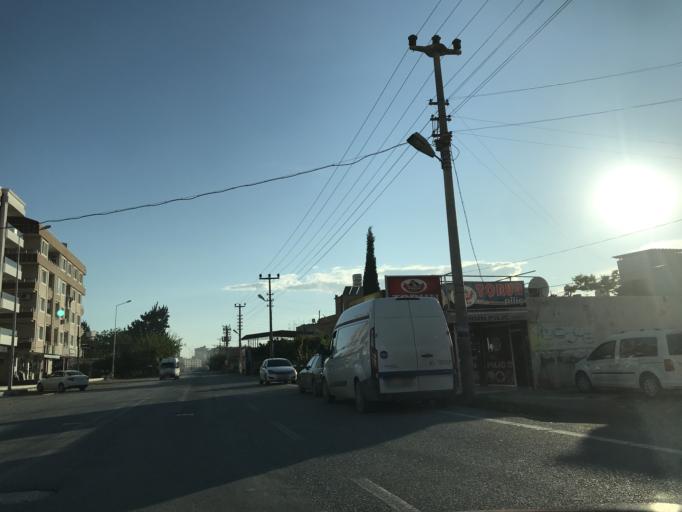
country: TR
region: Hatay
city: Iskenderun
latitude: 36.5717
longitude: 36.1554
